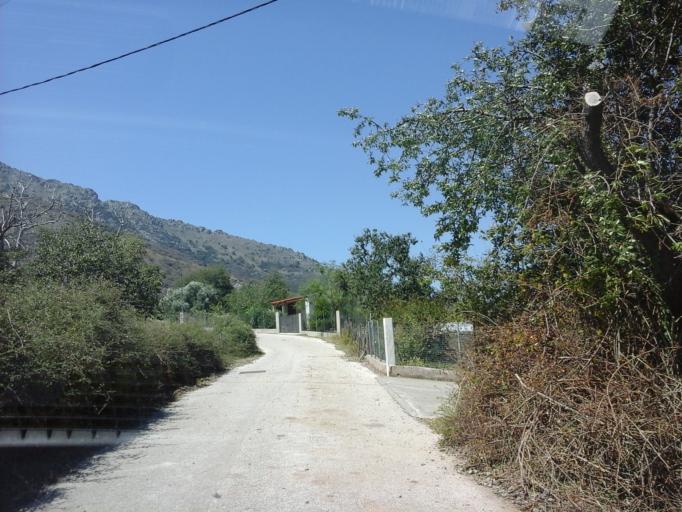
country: GR
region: East Macedonia and Thrace
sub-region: Nomos Evrou
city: Samothraki
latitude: 40.5028
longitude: 25.5699
